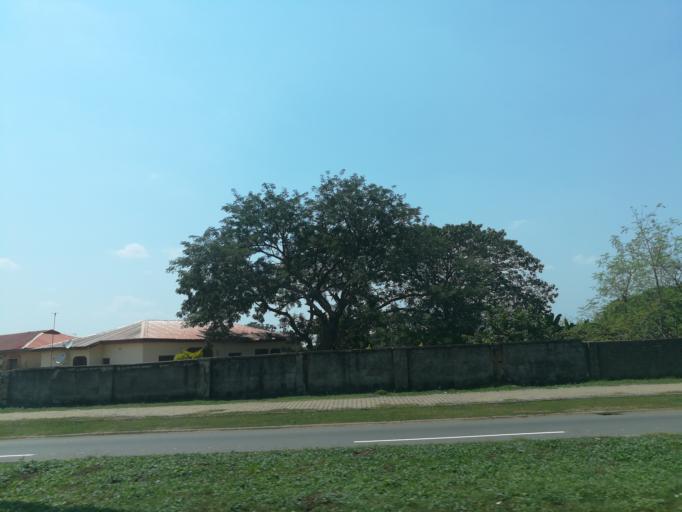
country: NG
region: Abuja Federal Capital Territory
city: Abuja
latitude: 9.0660
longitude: 7.4238
